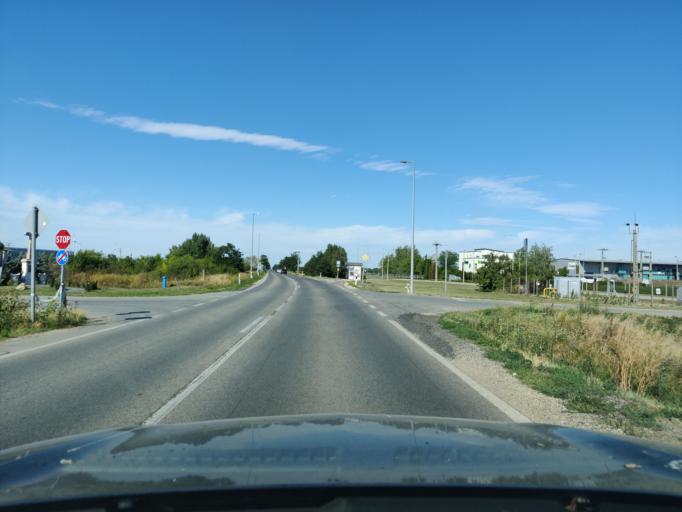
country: HU
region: Gyor-Moson-Sopron
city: Janossomorja
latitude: 47.8014
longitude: 17.1586
